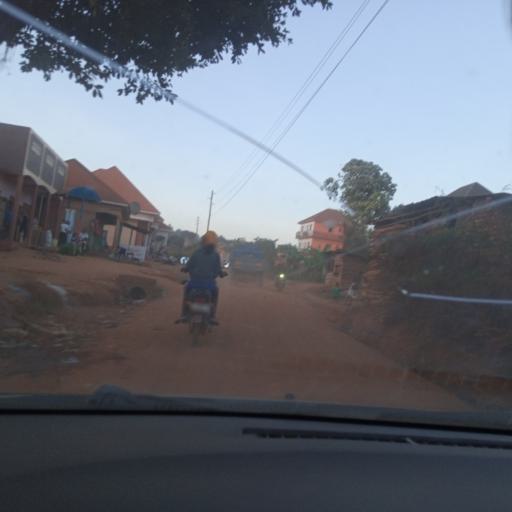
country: UG
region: Central Region
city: Masaka
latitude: -0.3193
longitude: 31.7673
